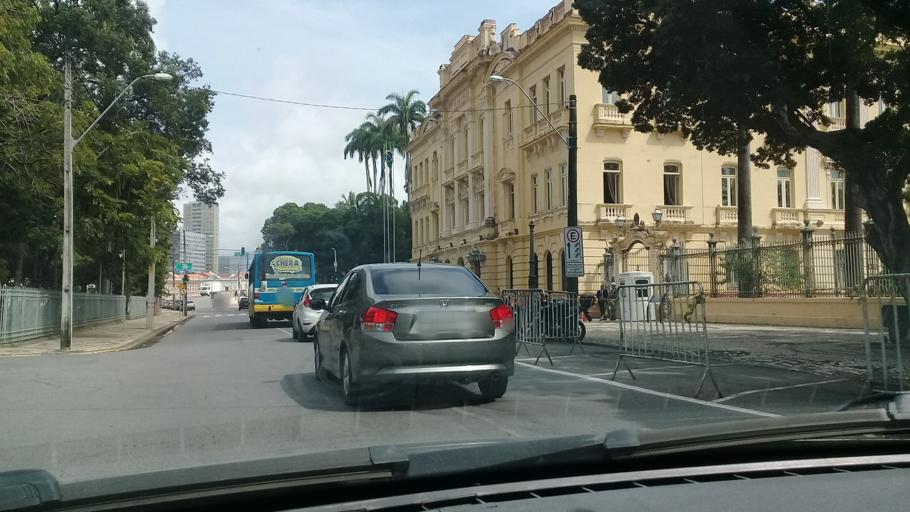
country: BR
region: Pernambuco
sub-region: Recife
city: Recife
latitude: -8.0605
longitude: -34.8770
